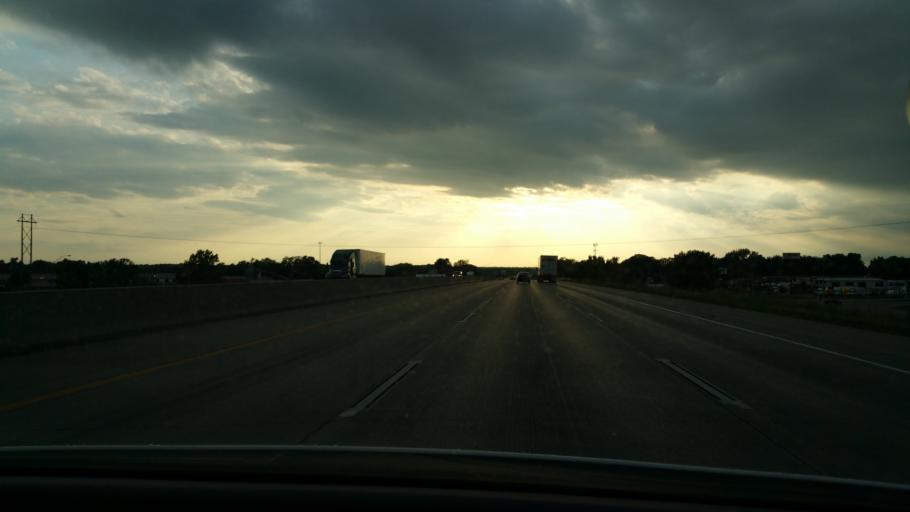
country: US
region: Iowa
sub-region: Polk County
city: Saylorville
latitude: 41.6496
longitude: -93.6171
